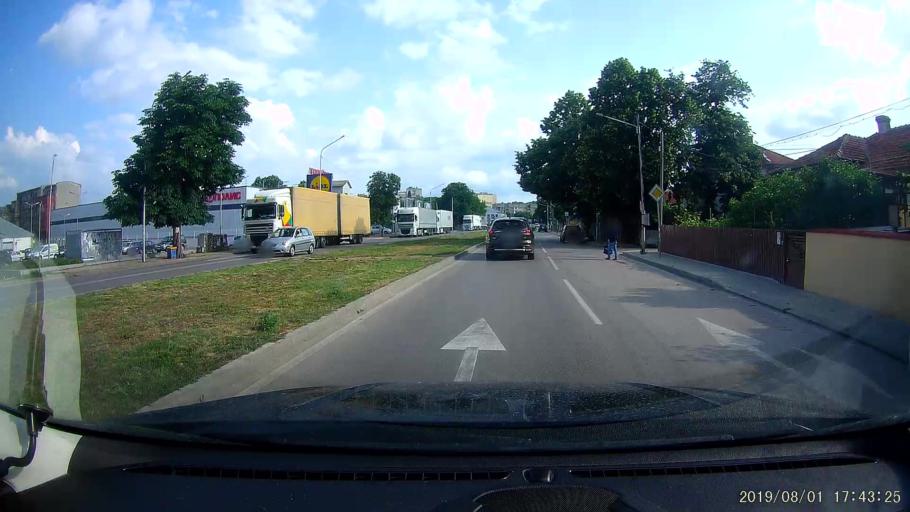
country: BG
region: Silistra
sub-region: Obshtina Silistra
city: Silistra
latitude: 44.1151
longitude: 27.2728
